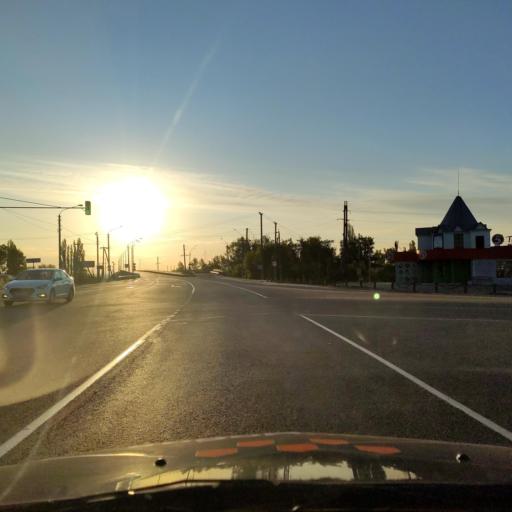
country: RU
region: Orjol
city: Livny
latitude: 52.4413
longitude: 37.5763
